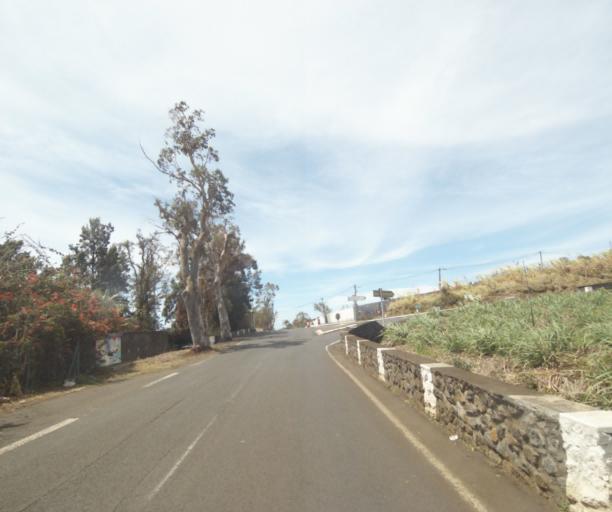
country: RE
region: Reunion
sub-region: Reunion
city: Saint-Paul
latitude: -21.0384
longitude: 55.2884
